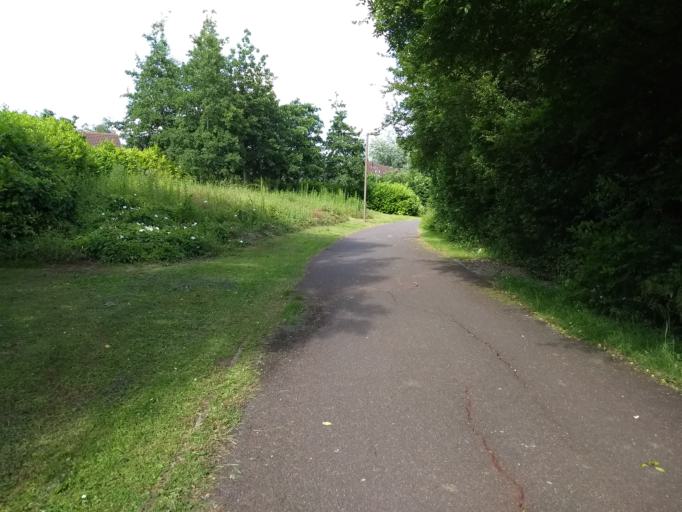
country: GB
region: England
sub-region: Milton Keynes
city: Shenley Church End
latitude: 52.0347
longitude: -0.8048
